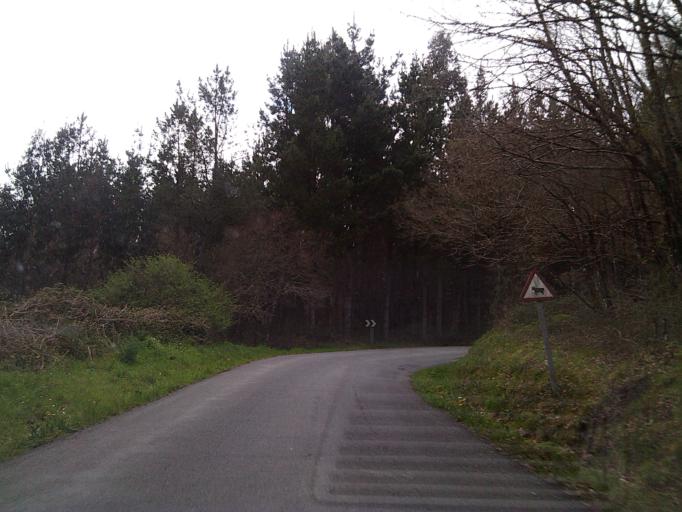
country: ES
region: Galicia
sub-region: Provincia de Lugo
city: Guitiriz
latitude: 43.1626
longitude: -7.8273
